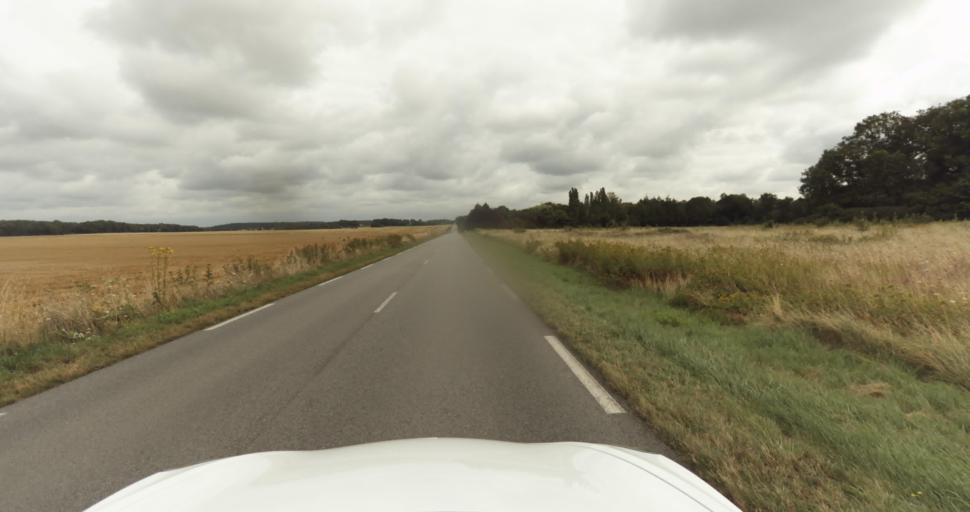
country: FR
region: Haute-Normandie
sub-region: Departement de l'Eure
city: Saint-Sebastien-de-Morsent
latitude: 49.0014
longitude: 1.0448
